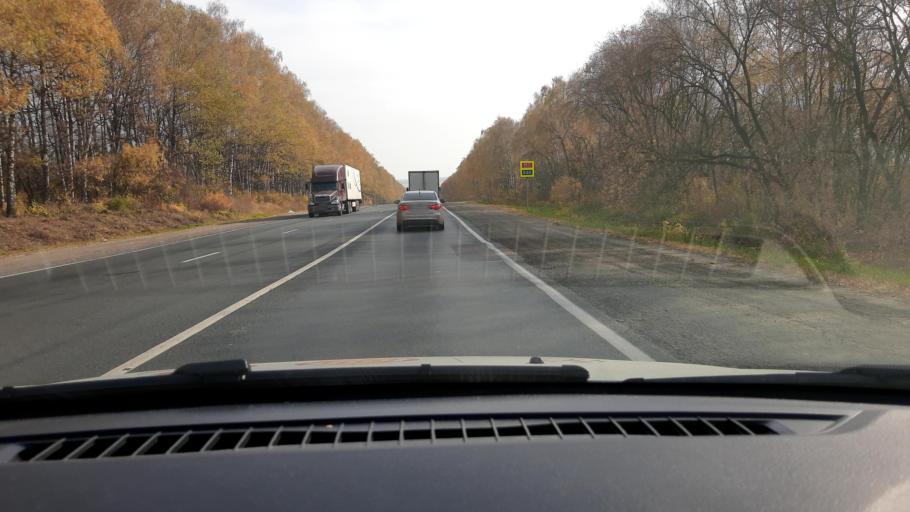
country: RU
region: Nizjnij Novgorod
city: Pamyat' Parizhskoy Kommuny
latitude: 56.0543
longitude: 44.4036
